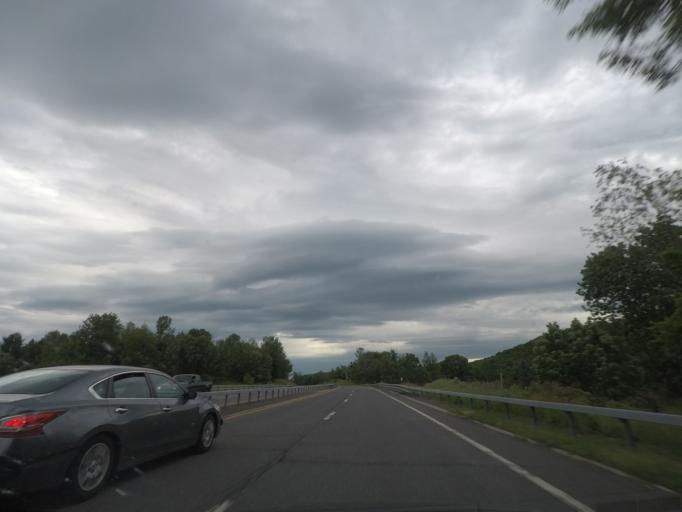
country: US
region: New York
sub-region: Dutchess County
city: Pine Plains
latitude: 42.0731
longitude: -73.7174
